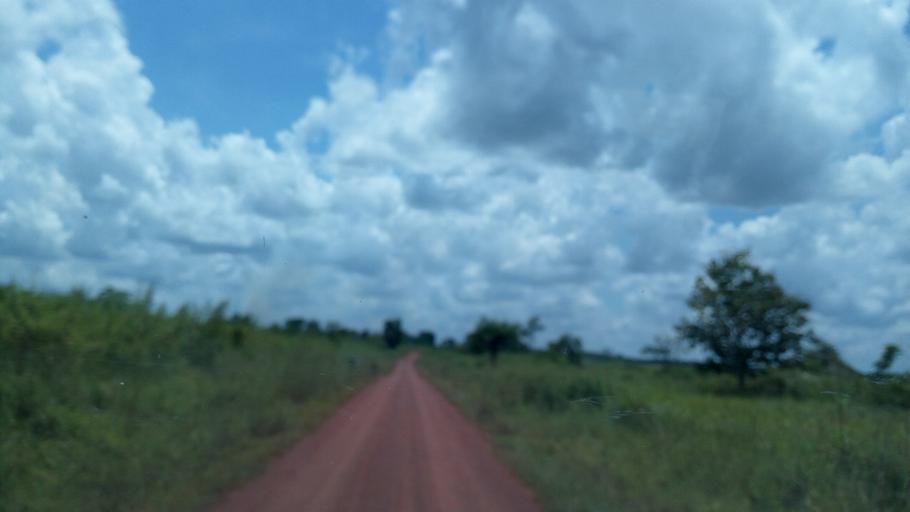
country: CD
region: Equateur
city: Libenge
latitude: 3.7731
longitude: 18.9412
